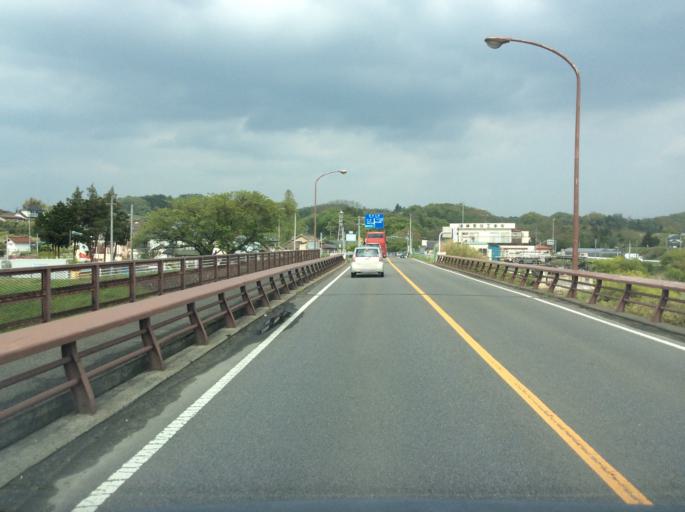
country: JP
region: Fukushima
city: Koriyama
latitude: 37.4226
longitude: 140.4152
